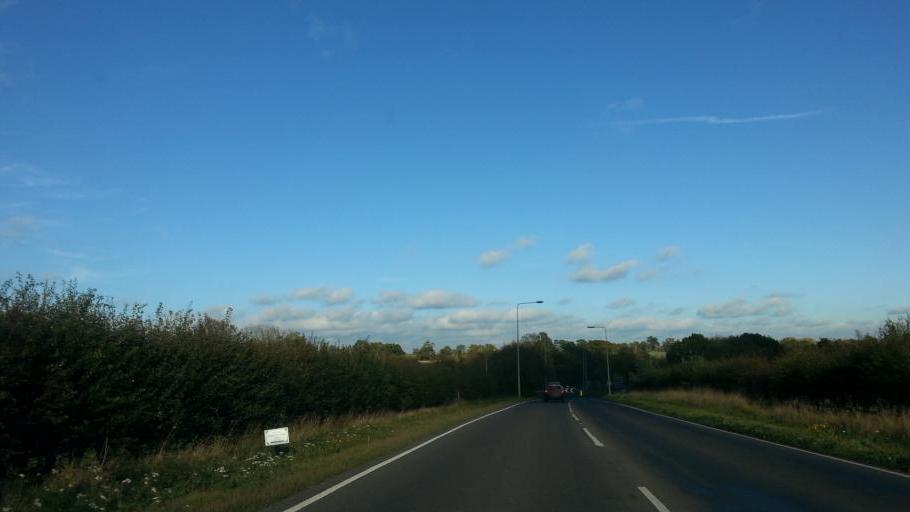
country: GB
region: England
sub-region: Norfolk
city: Harleston
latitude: 52.4091
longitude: 1.3183
